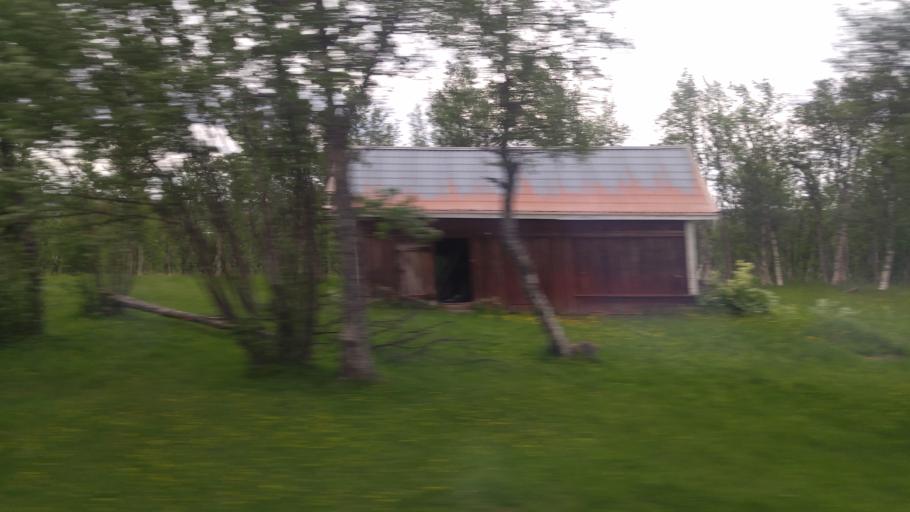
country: NO
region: Nord-Trondelag
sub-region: Meraker
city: Meraker
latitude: 63.3179
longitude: 12.1956
